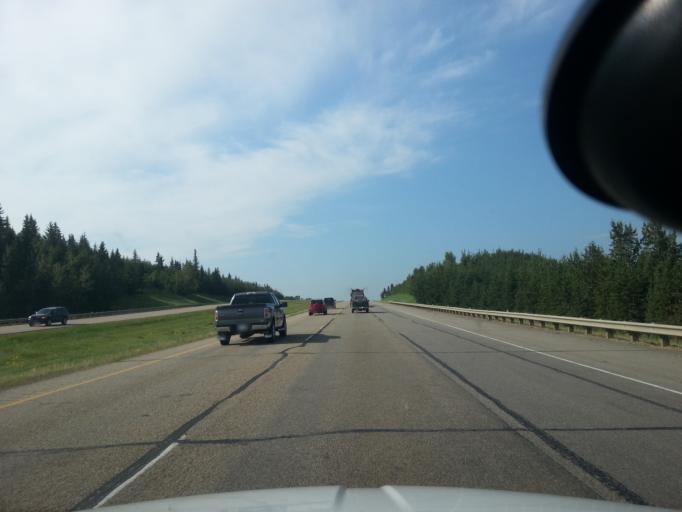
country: CA
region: Alberta
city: Blackfalds
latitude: 52.3560
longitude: -113.8370
